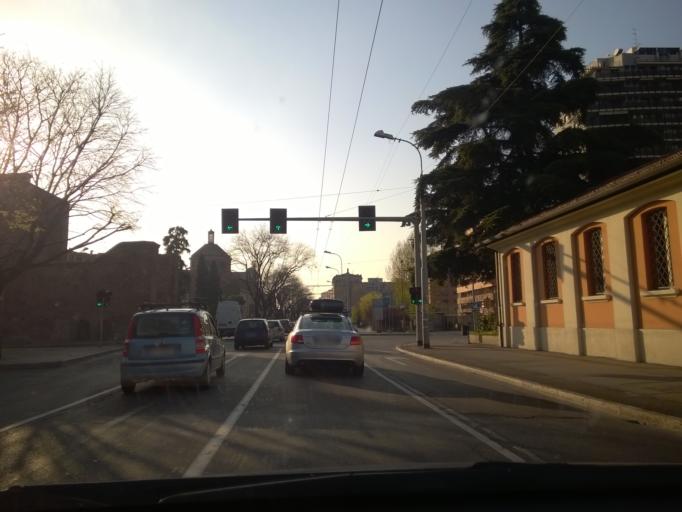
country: IT
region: Emilia-Romagna
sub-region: Provincia di Bologna
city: Bologna
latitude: 44.5022
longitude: 11.3532
